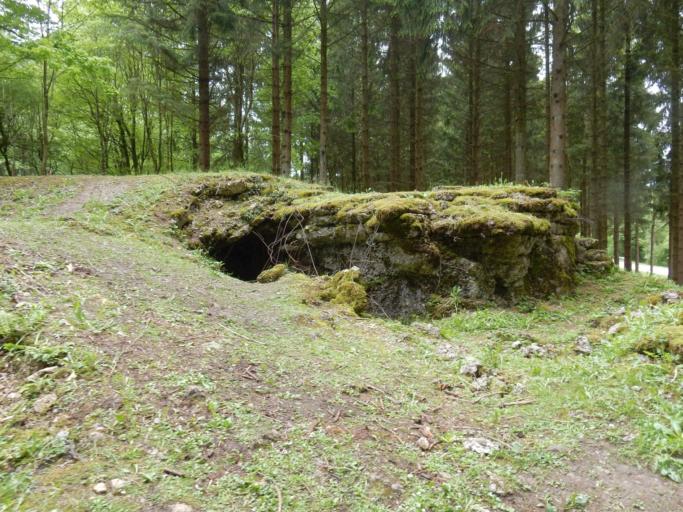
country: FR
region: Lorraine
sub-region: Departement de la Meuse
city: Verdun
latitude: 49.2113
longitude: 5.4310
